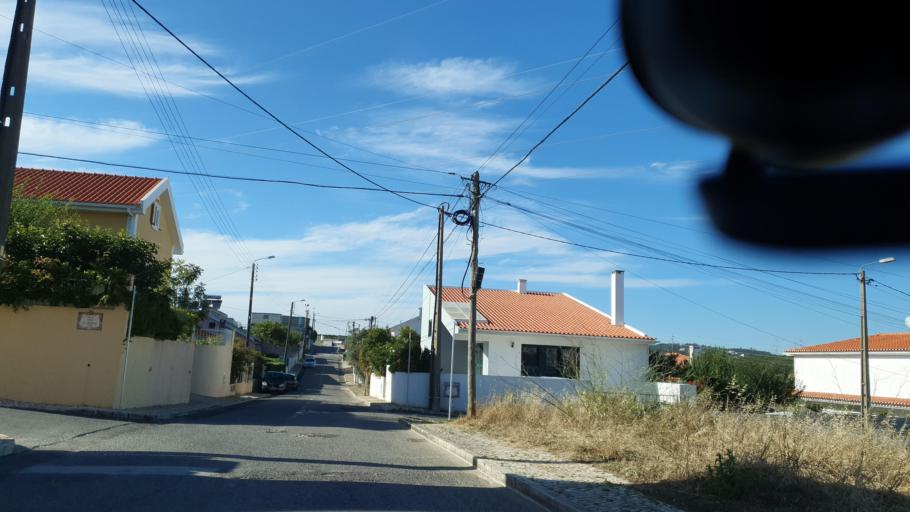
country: PT
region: Lisbon
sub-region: Sintra
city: Belas
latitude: 38.8018
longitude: -9.2534
